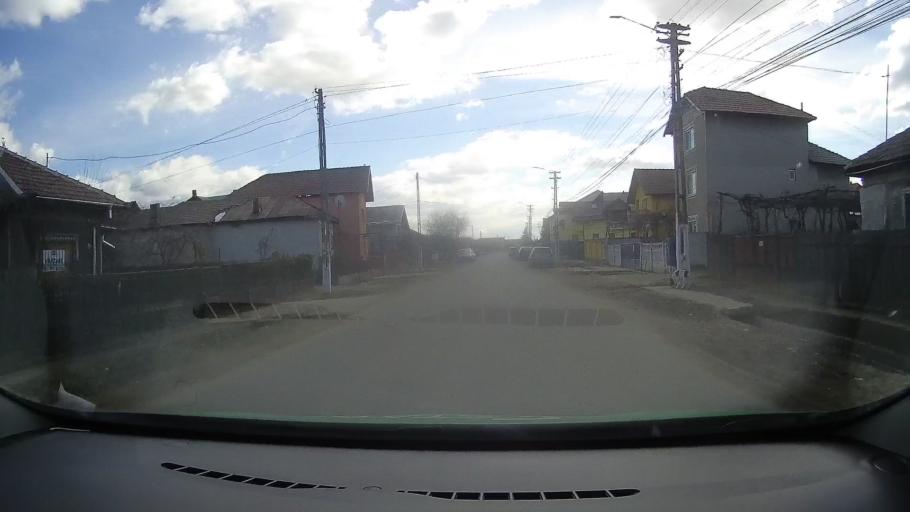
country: RO
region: Dambovita
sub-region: Comuna Doicesti
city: Doicesti
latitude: 44.9811
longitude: 25.3895
